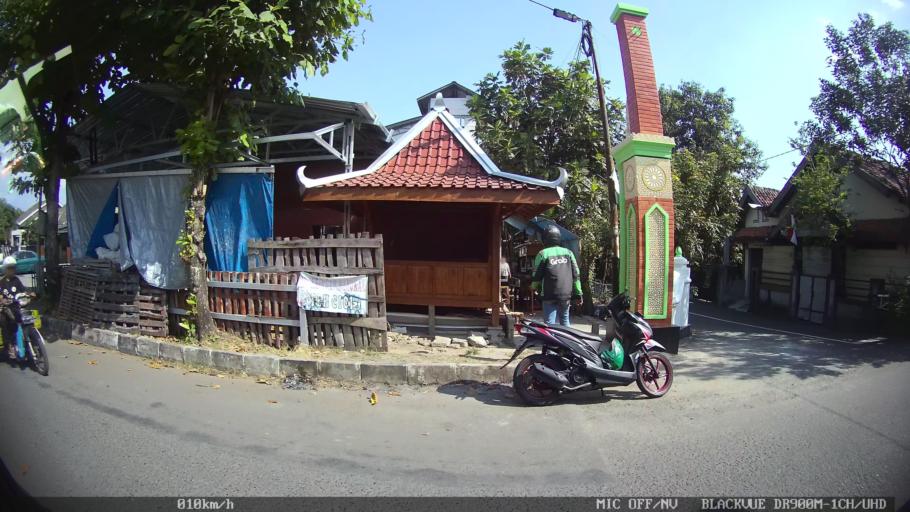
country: ID
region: Daerah Istimewa Yogyakarta
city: Sewon
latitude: -7.8325
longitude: 110.3927
